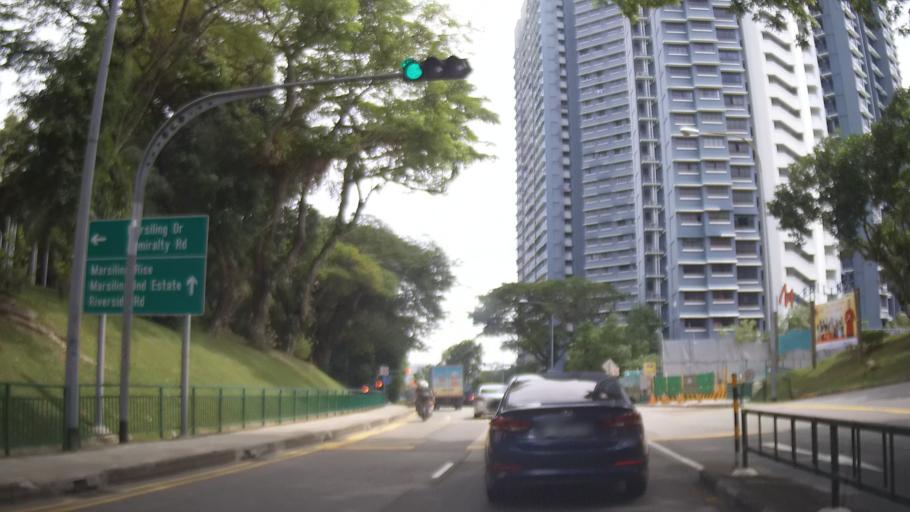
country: MY
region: Johor
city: Johor Bahru
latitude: 1.4391
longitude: 103.7771
